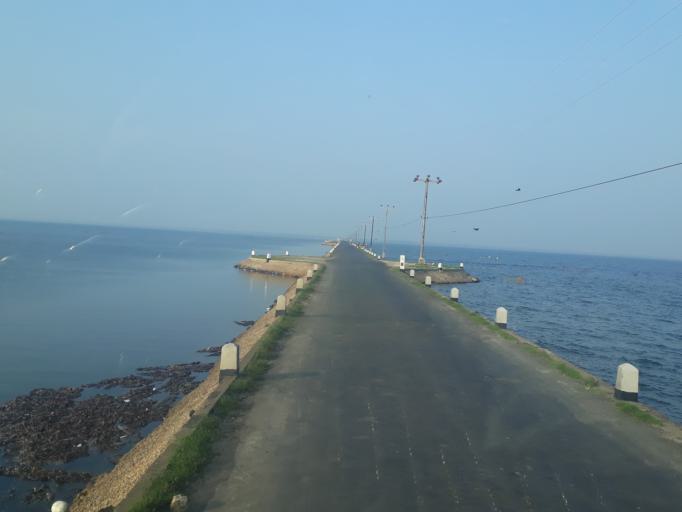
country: LK
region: Northern Province
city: Jaffna
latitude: 9.6226
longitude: 79.8907
